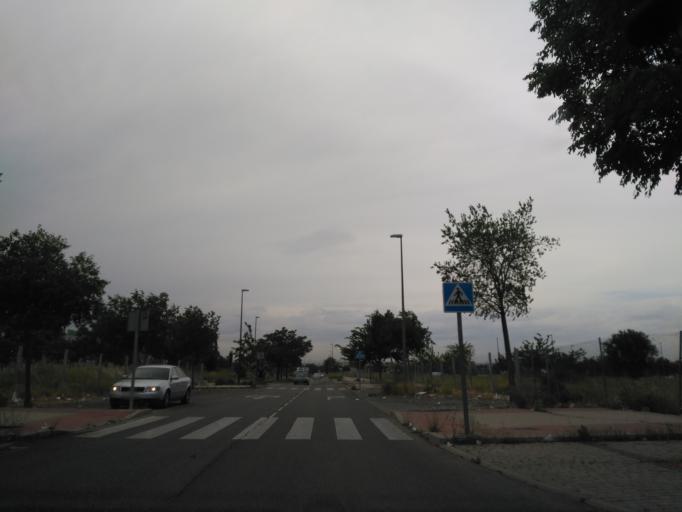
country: ES
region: Madrid
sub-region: Provincia de Madrid
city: Villaverde
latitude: 40.3338
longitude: -3.7179
